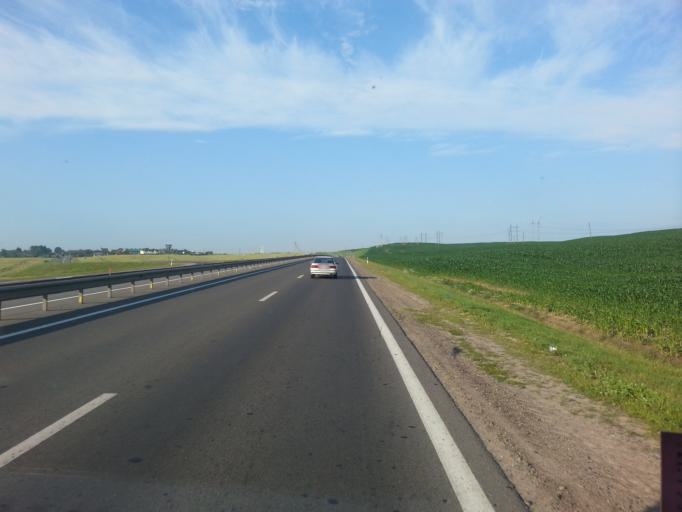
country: BY
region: Minsk
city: Bal'shavik
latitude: 54.0123
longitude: 27.5435
